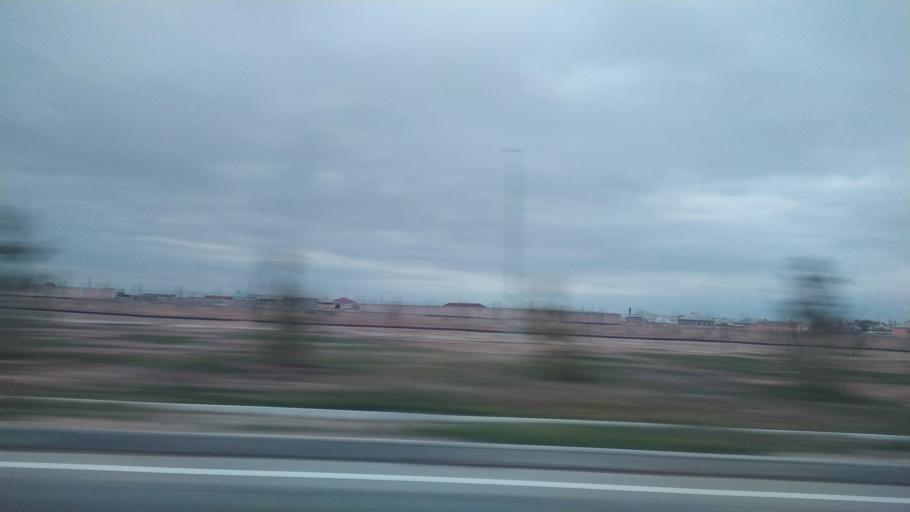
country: KZ
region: Ongtustik Qazaqstan
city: Turkestan
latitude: 43.2743
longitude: 68.4061
